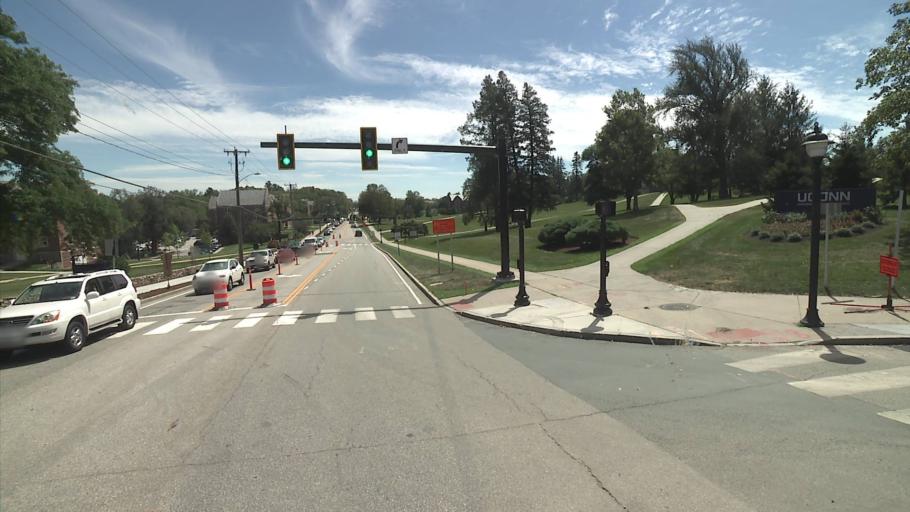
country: US
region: Connecticut
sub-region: Tolland County
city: Storrs
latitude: 41.8115
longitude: -72.2496
